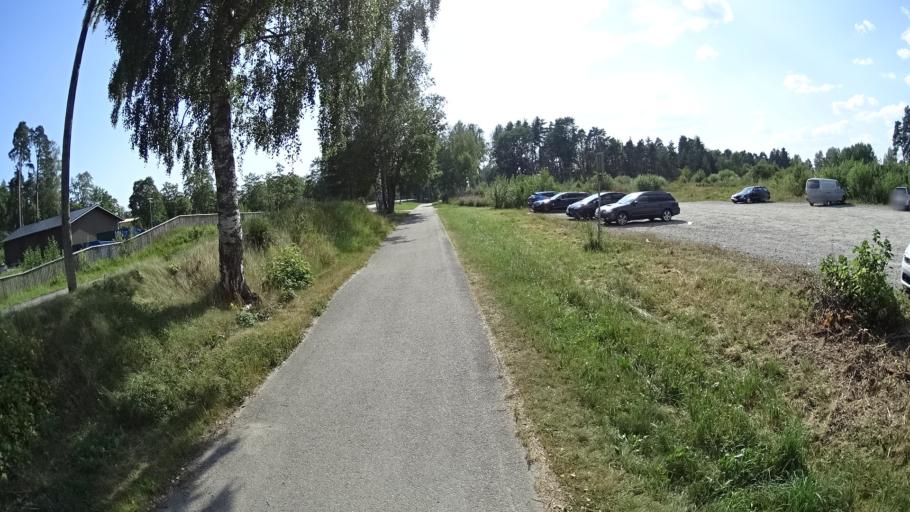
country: FI
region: Uusimaa
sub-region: Porvoo
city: Porvoo
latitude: 60.3940
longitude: 25.6451
